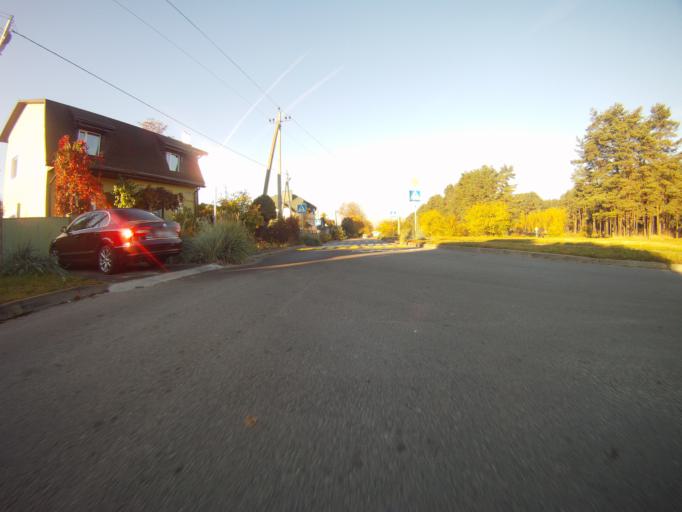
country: BY
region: Minsk
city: Minsk
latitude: 53.9476
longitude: 27.5800
